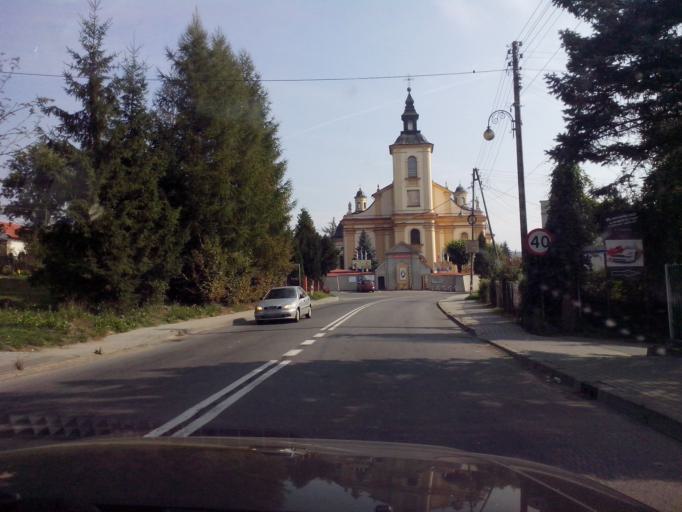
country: PL
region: Subcarpathian Voivodeship
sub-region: Powiat strzyzowski
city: Czudec
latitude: 49.9456
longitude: 21.8344
